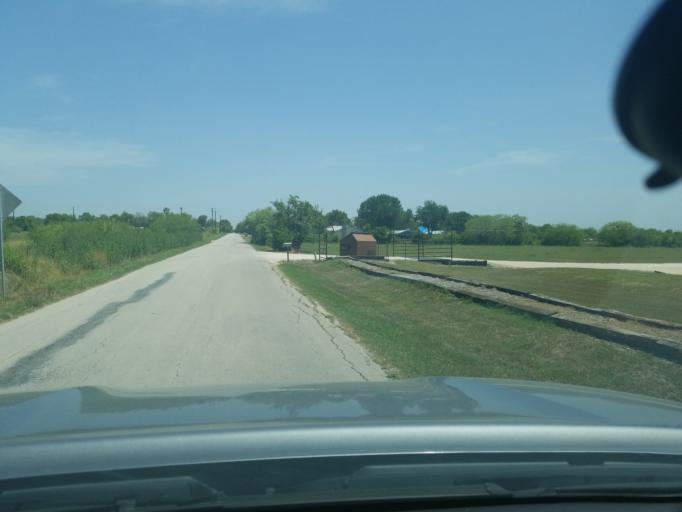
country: US
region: Texas
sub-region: Guadalupe County
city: Cibolo
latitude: 29.5816
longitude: -98.1991
